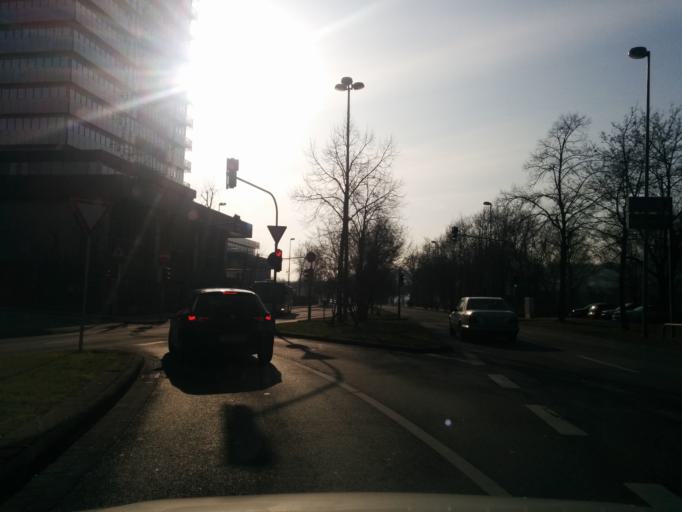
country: DE
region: Rheinland-Pfalz
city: Koblenz
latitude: 50.3611
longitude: 7.5684
